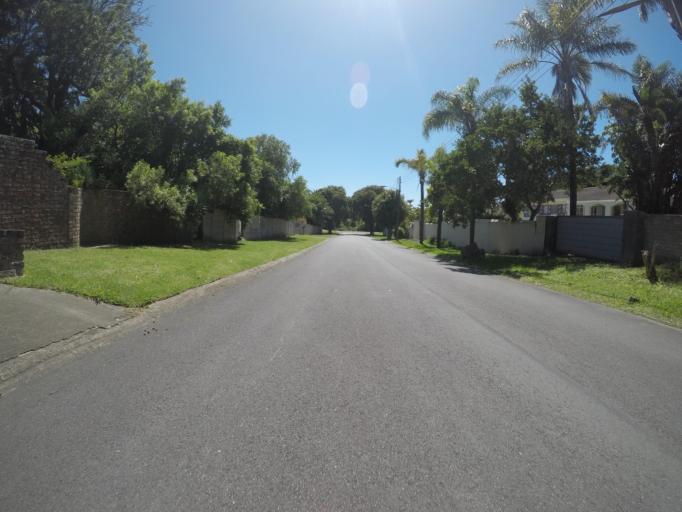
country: ZA
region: Eastern Cape
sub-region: Buffalo City Metropolitan Municipality
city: East London
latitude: -32.9741
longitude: 27.9430
